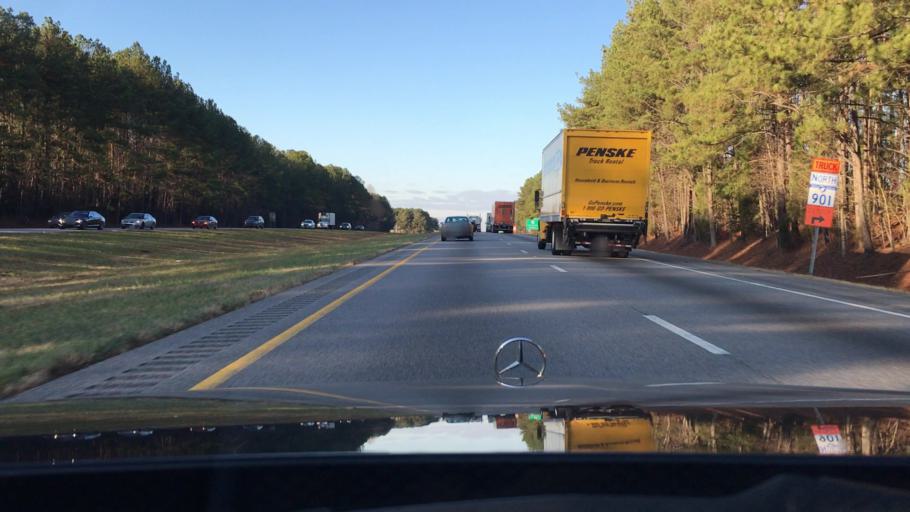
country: US
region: South Carolina
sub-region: Chester County
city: Eureka Mill
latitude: 34.7378
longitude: -81.0347
